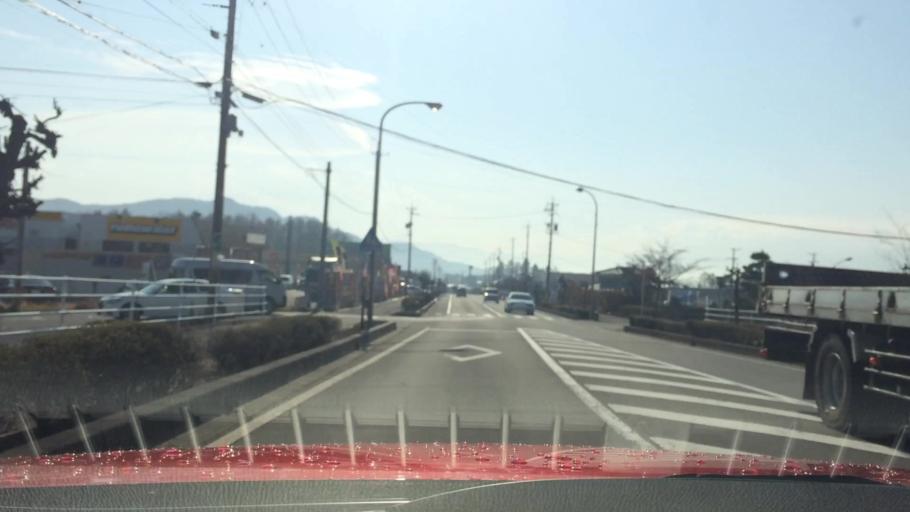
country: JP
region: Nagano
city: Komoro
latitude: 36.3271
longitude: 138.5089
